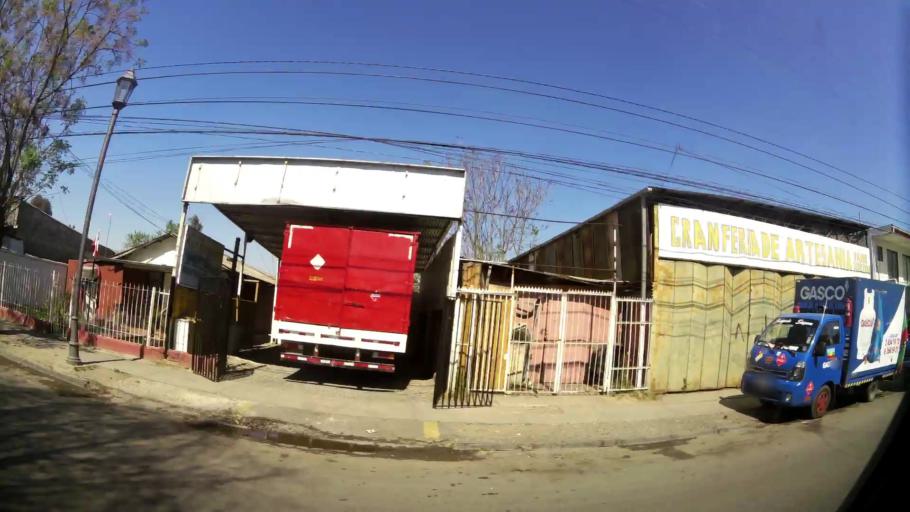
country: CL
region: Santiago Metropolitan
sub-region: Provincia de Talagante
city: Penaflor
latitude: -33.5685
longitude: -70.8028
